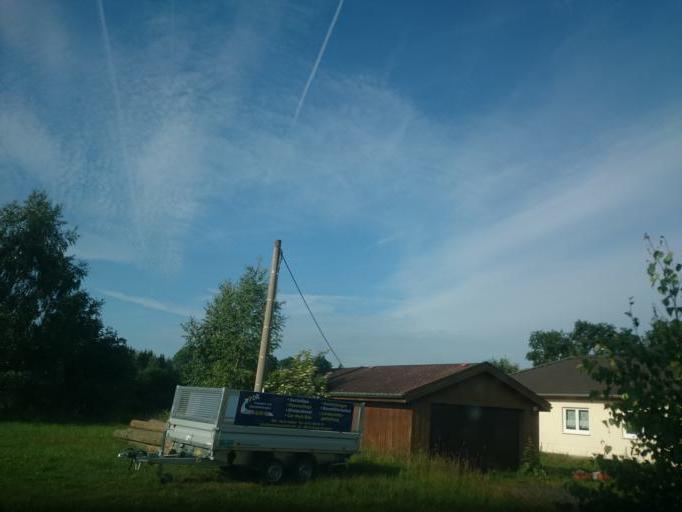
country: DE
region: Saxony
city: Brand-Erbisdorf
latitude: 50.8738
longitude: 13.2934
